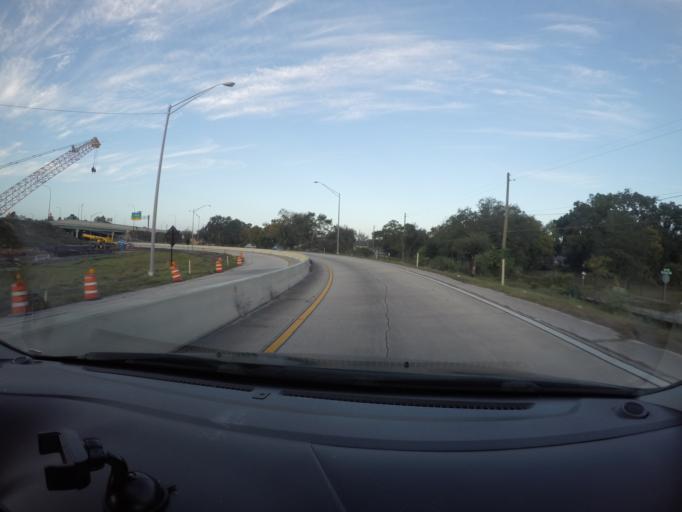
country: US
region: Florida
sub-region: Orange County
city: Orlando
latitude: 28.5364
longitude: -81.3867
